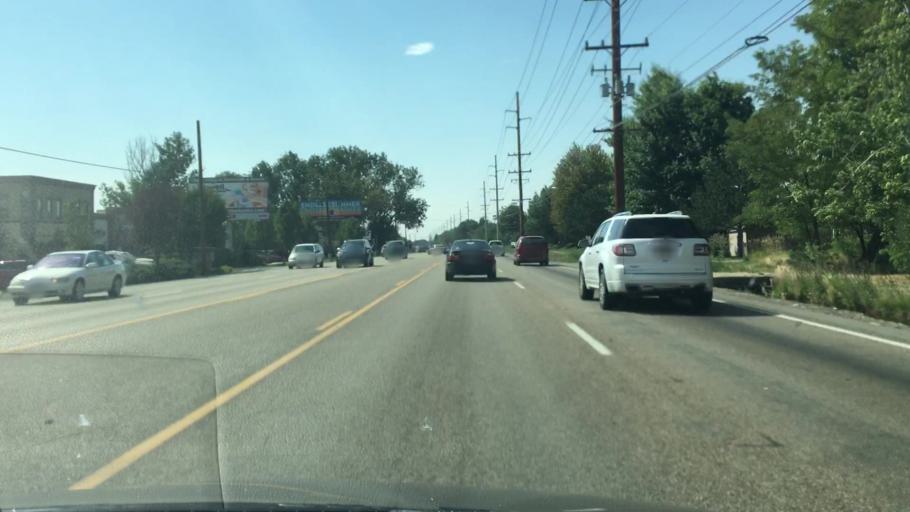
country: US
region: Idaho
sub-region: Ada County
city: Eagle
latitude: 43.6773
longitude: -116.2988
